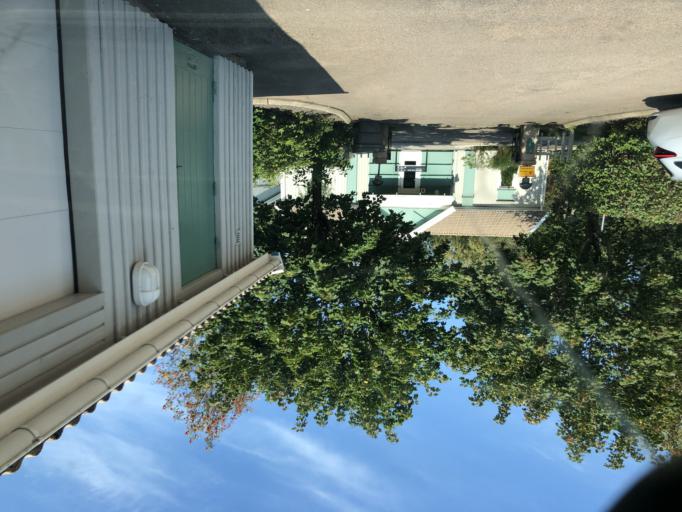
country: SE
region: Vaestra Goetaland
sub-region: Goteborg
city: Goeteborg
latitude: 57.7594
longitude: 11.9704
